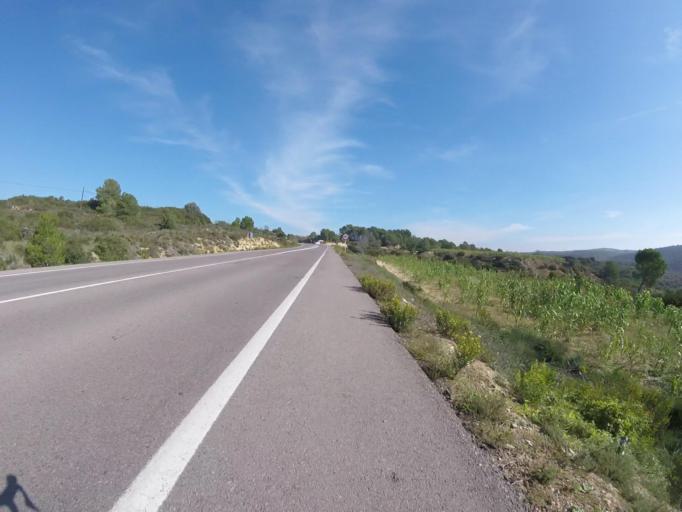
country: ES
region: Valencia
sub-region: Provincia de Castello
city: Benlloch
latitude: 40.2567
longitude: 0.0771
